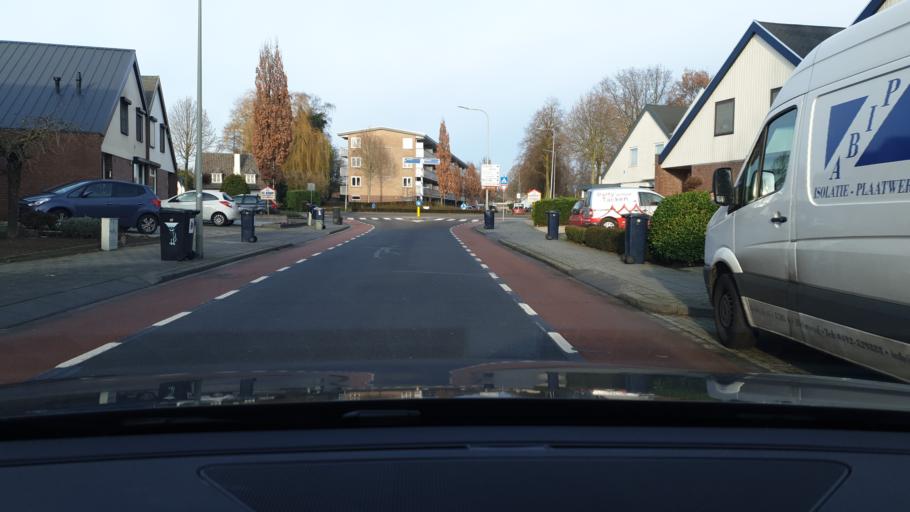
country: NL
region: Limburg
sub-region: Gemeente Venray
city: Venray
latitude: 51.4574
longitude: 6.0469
